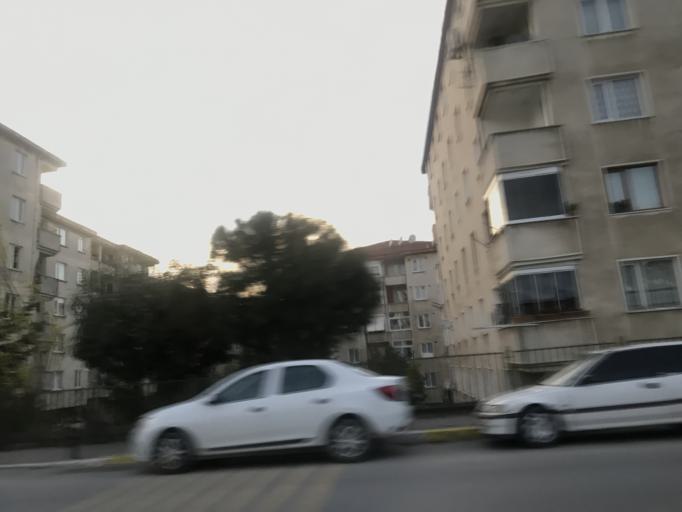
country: TR
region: Istanbul
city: Umraniye
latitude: 41.0331
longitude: 29.0966
